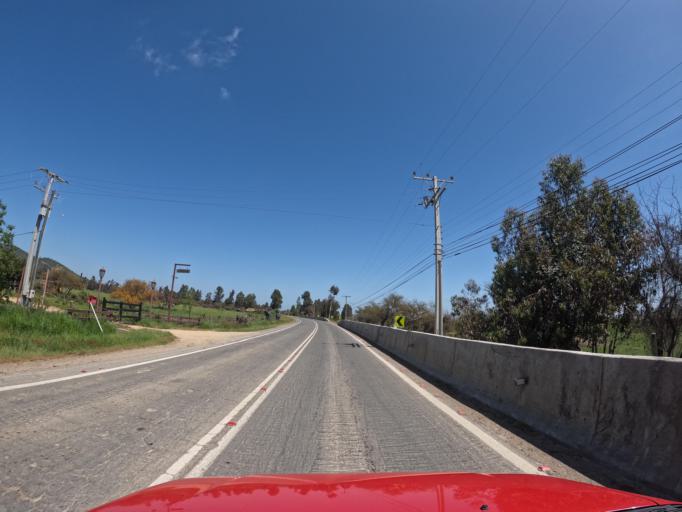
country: CL
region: O'Higgins
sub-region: Provincia de Colchagua
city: Santa Cruz
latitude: -34.7306
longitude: -71.6769
